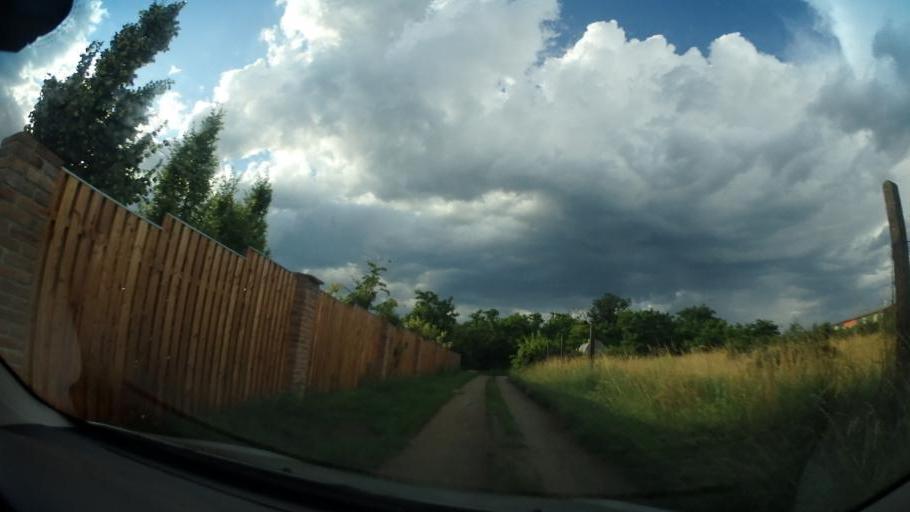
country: CZ
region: South Moravian
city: Dolni Kounice
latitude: 49.0555
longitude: 16.4917
